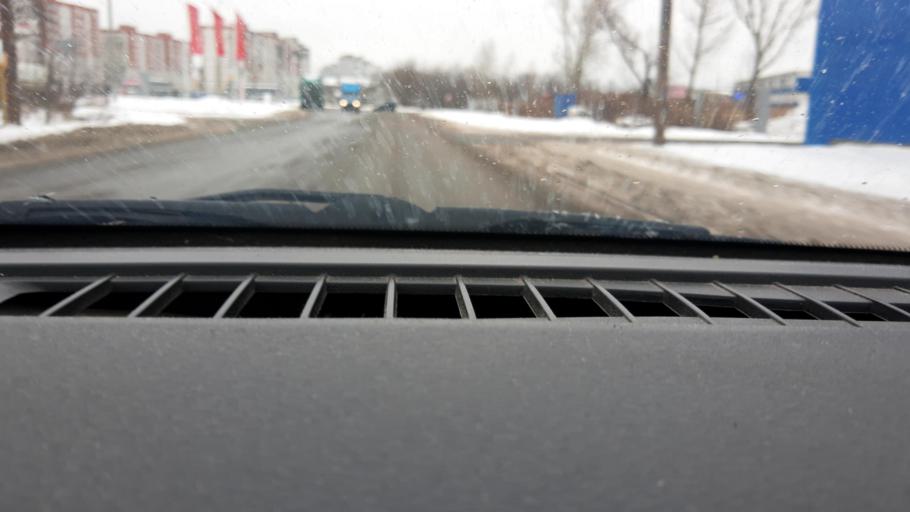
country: RU
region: Nizjnij Novgorod
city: Gorbatovka
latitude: 56.3391
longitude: 43.8065
